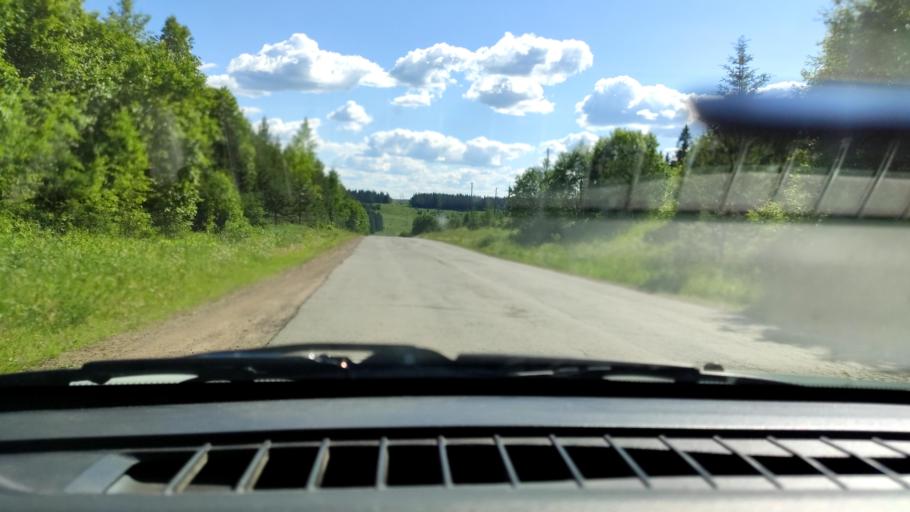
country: RU
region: Perm
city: Uinskoye
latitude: 57.1236
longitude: 56.5544
